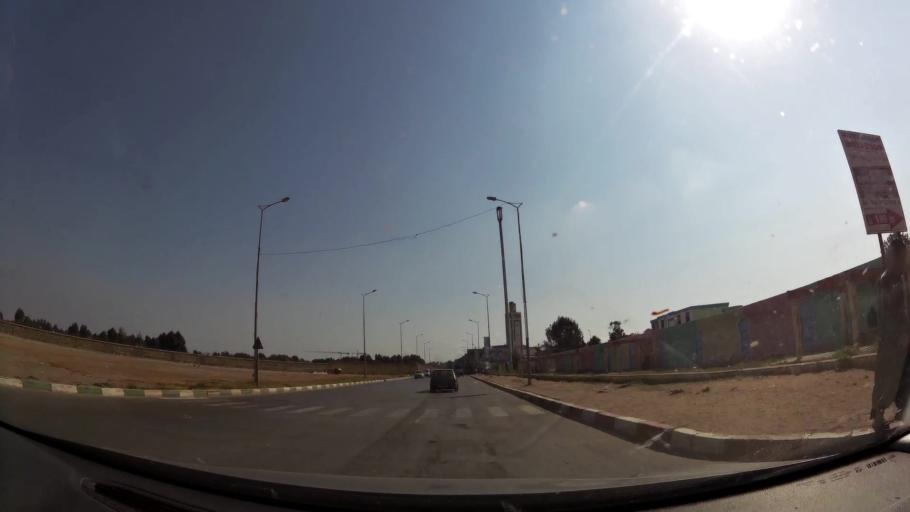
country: MA
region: Rabat-Sale-Zemmour-Zaer
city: Sale
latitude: 34.0597
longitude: -6.7685
